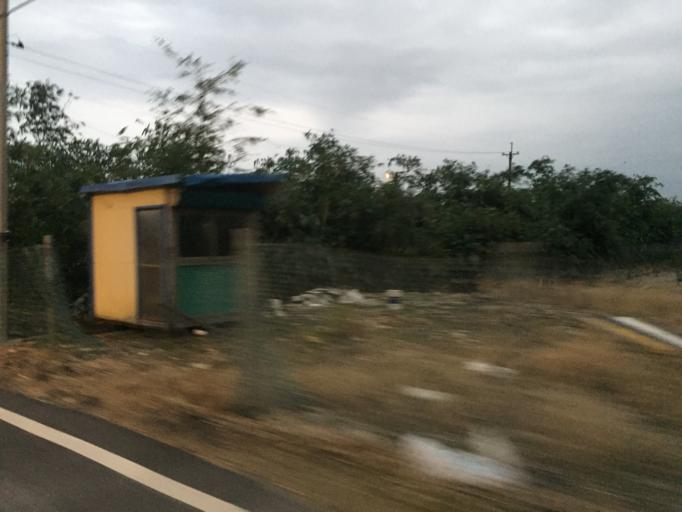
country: TW
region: Taiwan
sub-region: Yilan
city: Yilan
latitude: 24.7642
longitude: 121.7373
